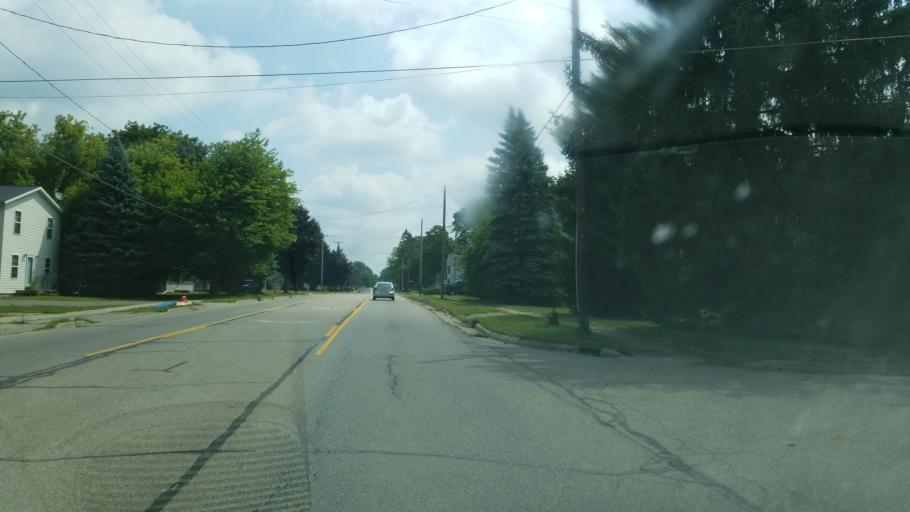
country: US
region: Michigan
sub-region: Kent County
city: Cedar Springs
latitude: 43.2199
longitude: -85.5599
